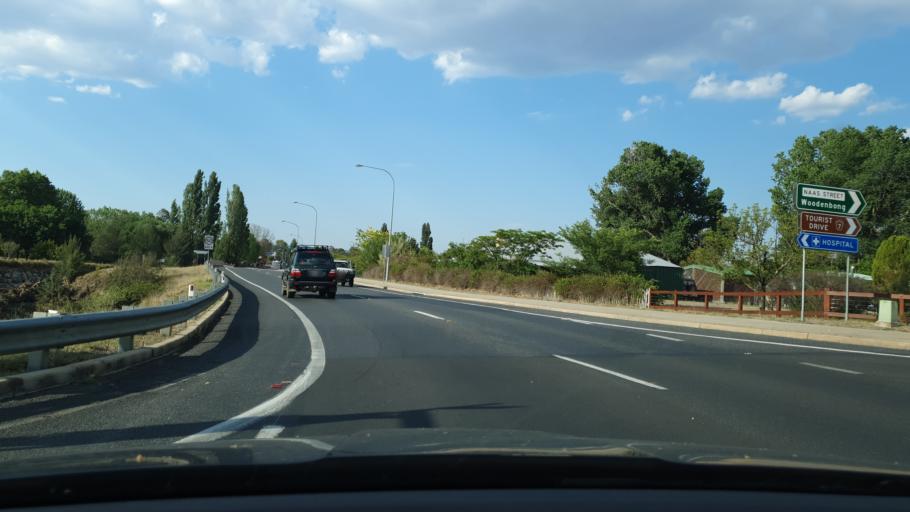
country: AU
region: New South Wales
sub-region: Tenterfield Municipality
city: Carrolls Creek
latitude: -29.0456
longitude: 152.0207
